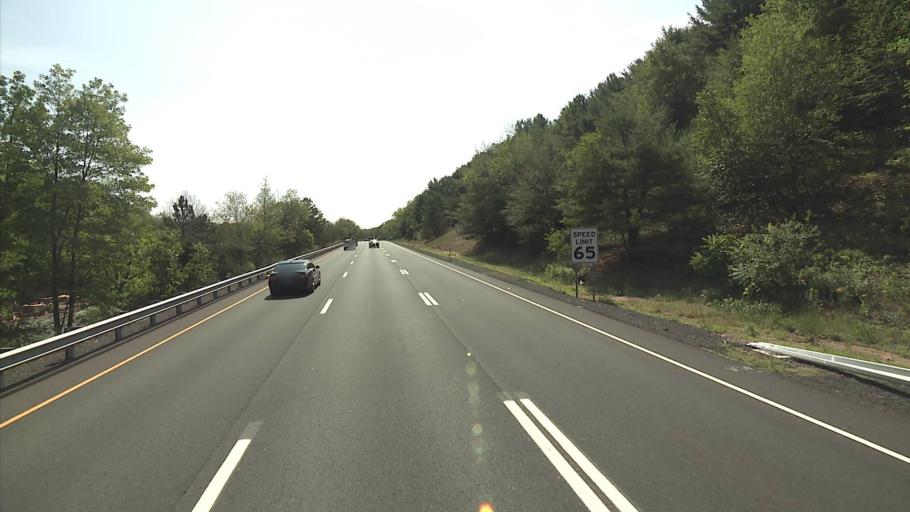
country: US
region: Connecticut
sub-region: Hartford County
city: Terramuggus
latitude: 41.6617
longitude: -72.5229
